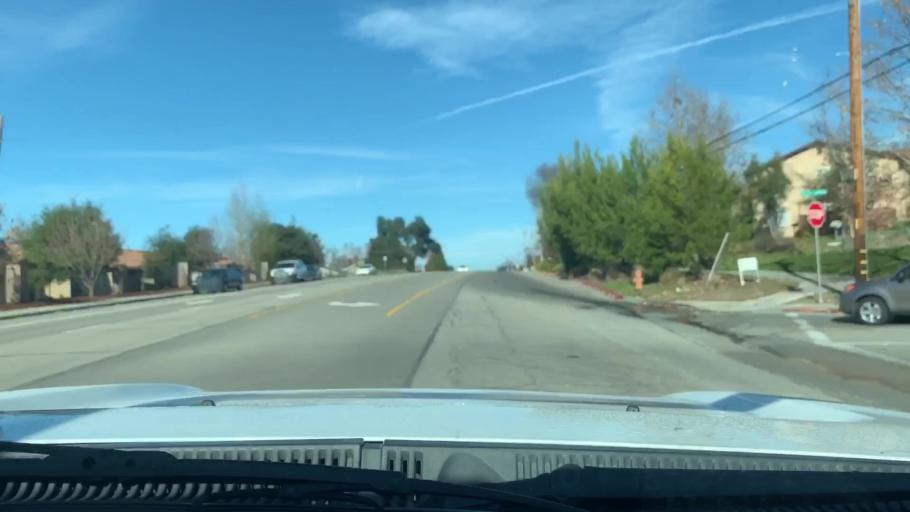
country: US
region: California
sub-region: San Luis Obispo County
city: Atascadero
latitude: 35.4548
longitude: -120.6395
